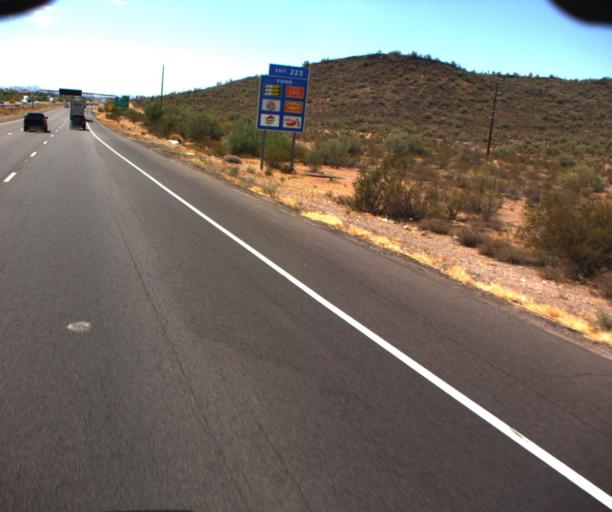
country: US
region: Arizona
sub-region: Maricopa County
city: Anthem
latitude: 33.8156
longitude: -112.1401
